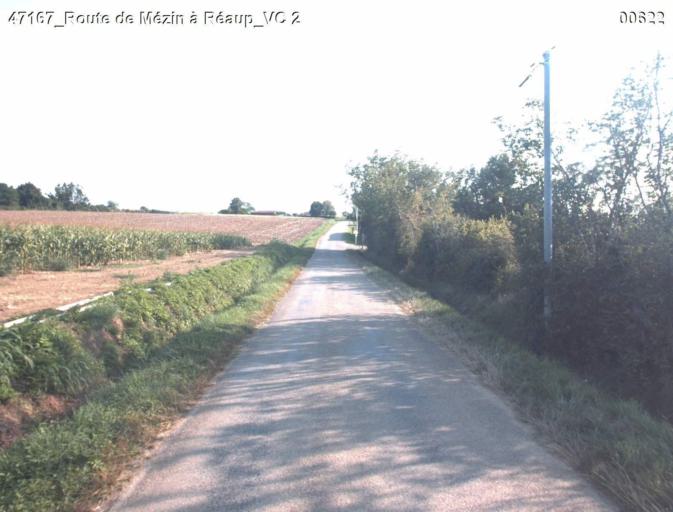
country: FR
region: Aquitaine
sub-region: Departement du Lot-et-Garonne
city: Mezin
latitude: 44.0631
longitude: 0.2566
